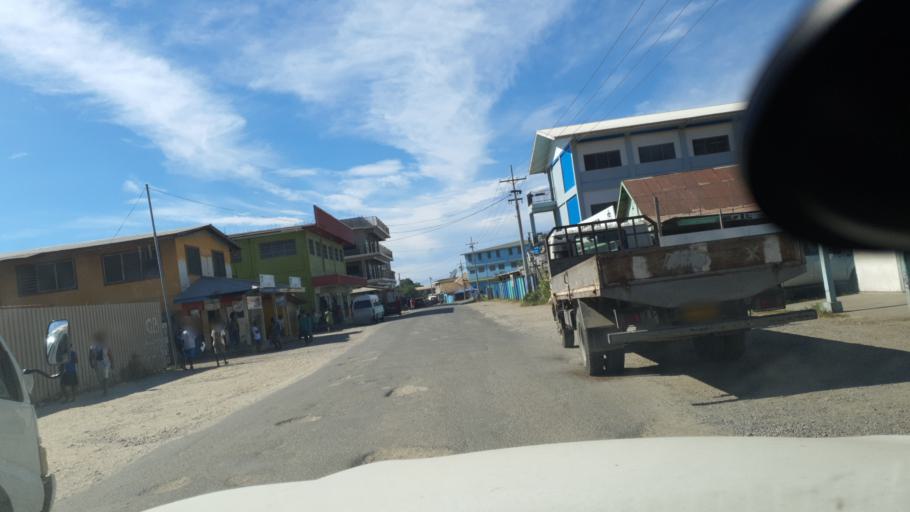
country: SB
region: Guadalcanal
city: Honiara
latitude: -9.4380
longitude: 159.9664
